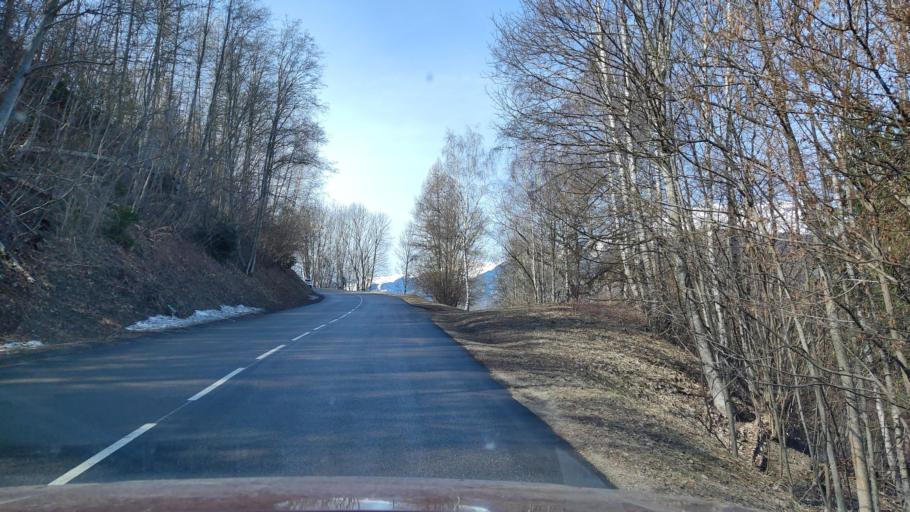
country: FR
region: Rhone-Alpes
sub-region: Departement de la Savoie
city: Macot-la-Plagne
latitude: 45.5644
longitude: 6.7192
